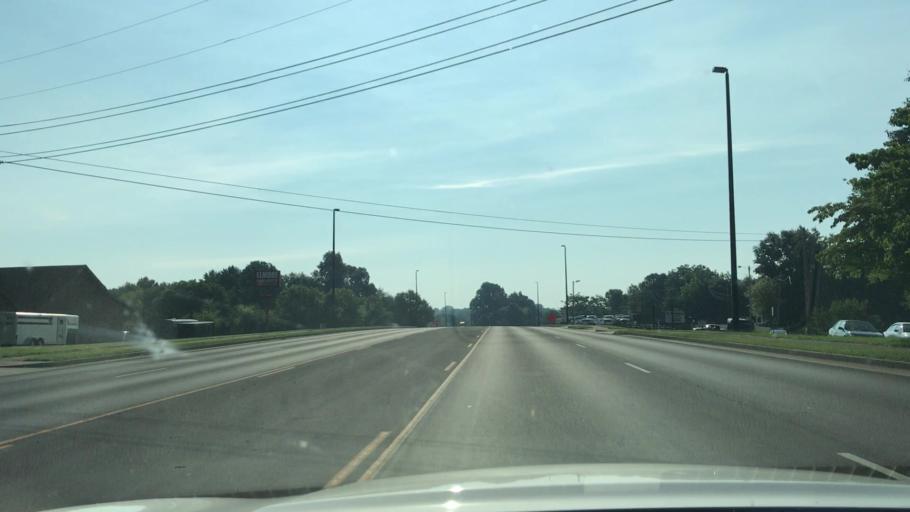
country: US
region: Kentucky
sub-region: Barren County
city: Glasgow
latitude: 37.0101
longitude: -85.9453
